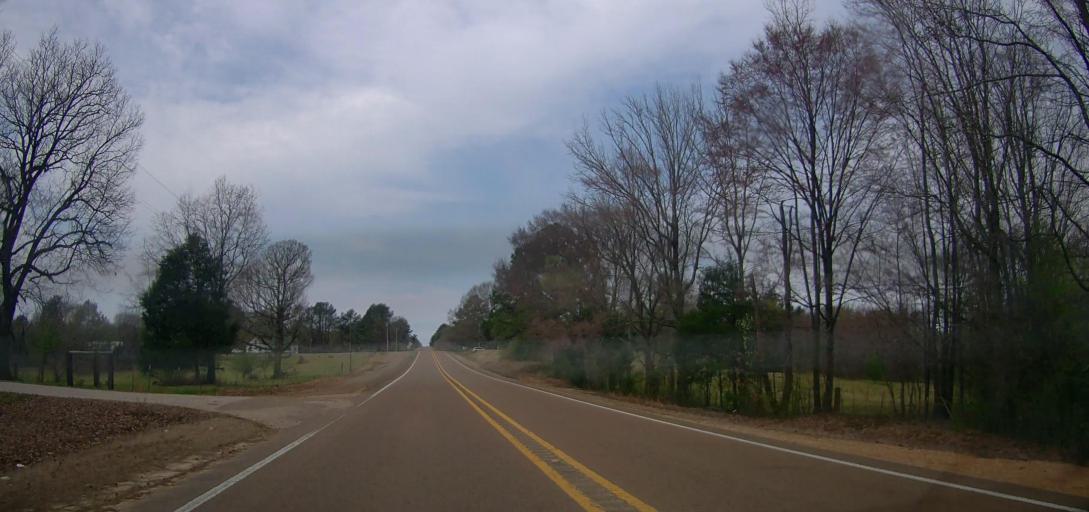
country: US
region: Mississippi
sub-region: Marshall County
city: Byhalia
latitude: 34.8362
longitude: -89.5884
